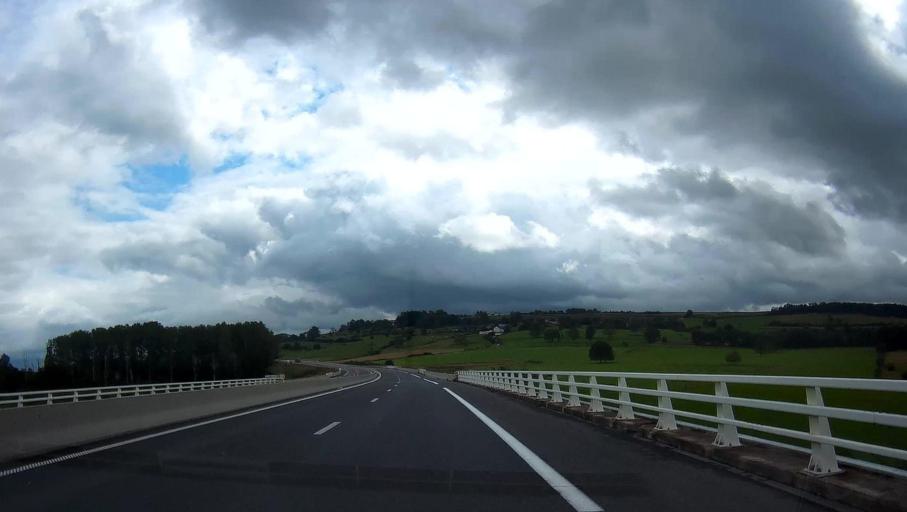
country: FR
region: Champagne-Ardenne
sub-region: Departement des Ardennes
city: Rimogne
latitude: 49.7963
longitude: 4.5368
